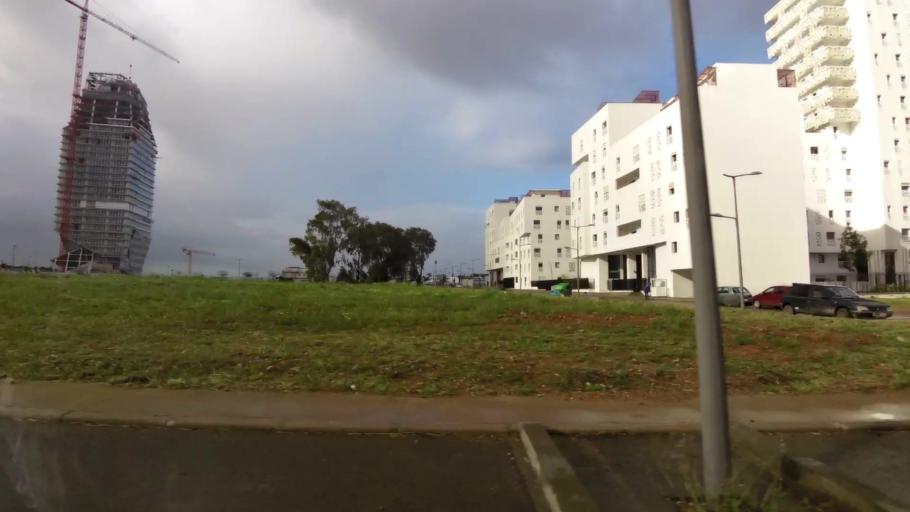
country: MA
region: Grand Casablanca
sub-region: Casablanca
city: Casablanca
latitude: 33.5663
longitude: -7.6612
